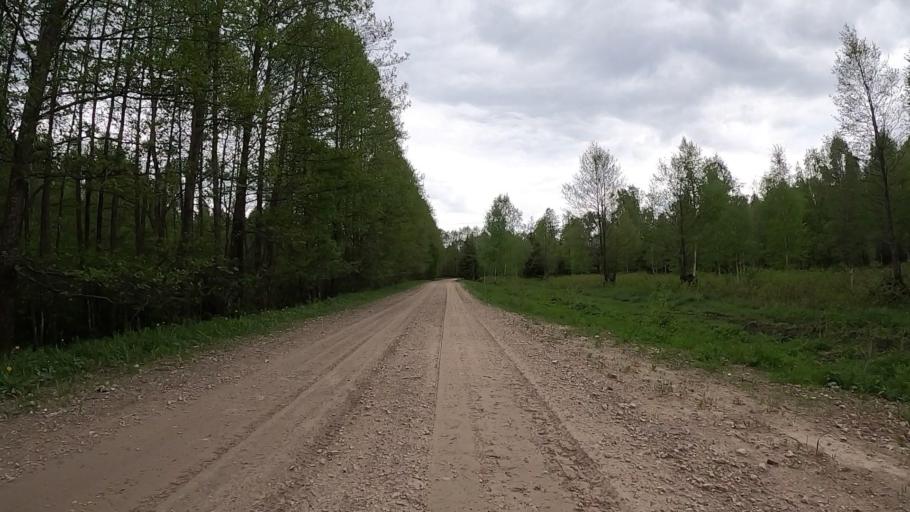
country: LV
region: Ozolnieku
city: Ozolnieki
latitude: 56.7898
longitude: 23.7762
